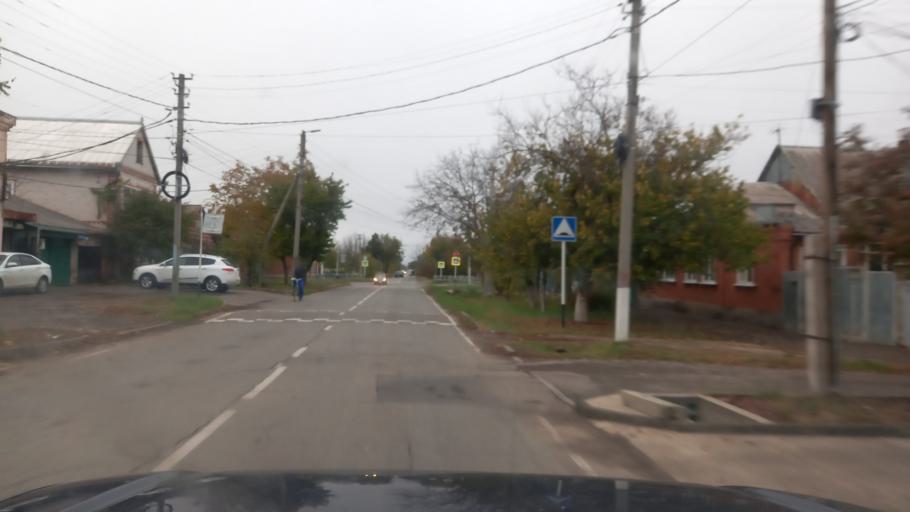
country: RU
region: Adygeya
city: Maykop
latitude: 44.6162
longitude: 40.1031
